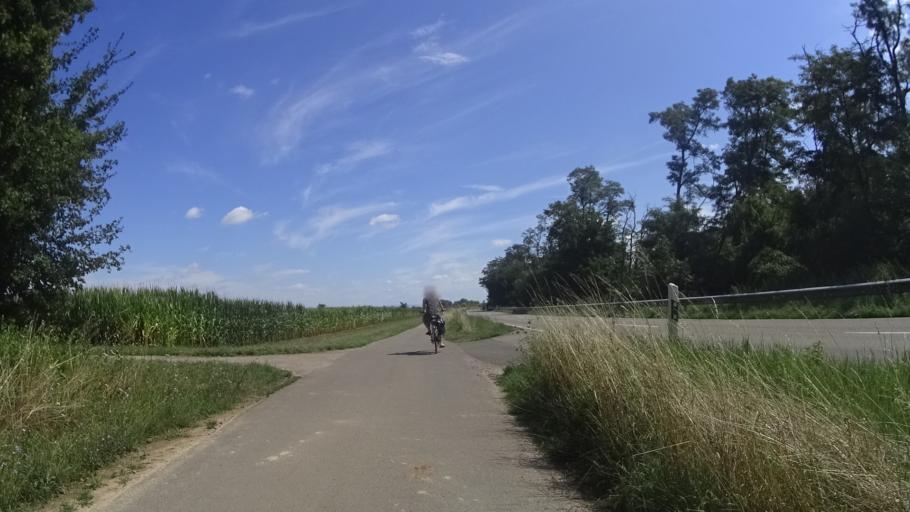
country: DE
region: Rheinland-Pfalz
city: Lingenfeld
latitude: 49.2581
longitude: 8.3578
